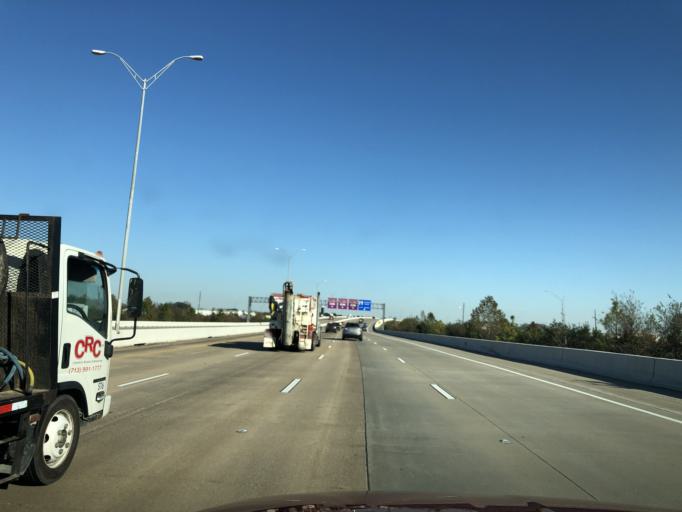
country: US
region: Texas
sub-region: Fort Bend County
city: Fresno
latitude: 29.5965
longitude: -95.4330
